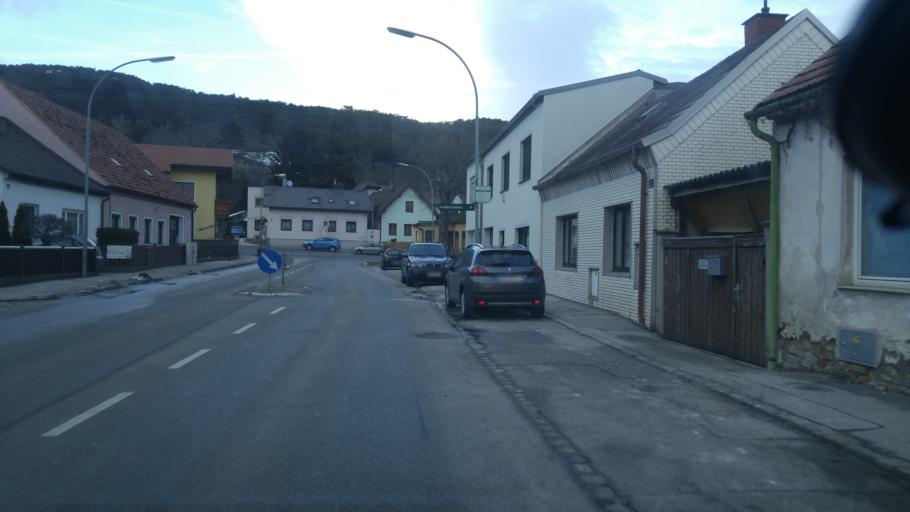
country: AT
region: Lower Austria
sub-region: Politischer Bezirk Baden
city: Bad Voslau
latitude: 47.9622
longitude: 16.1922
